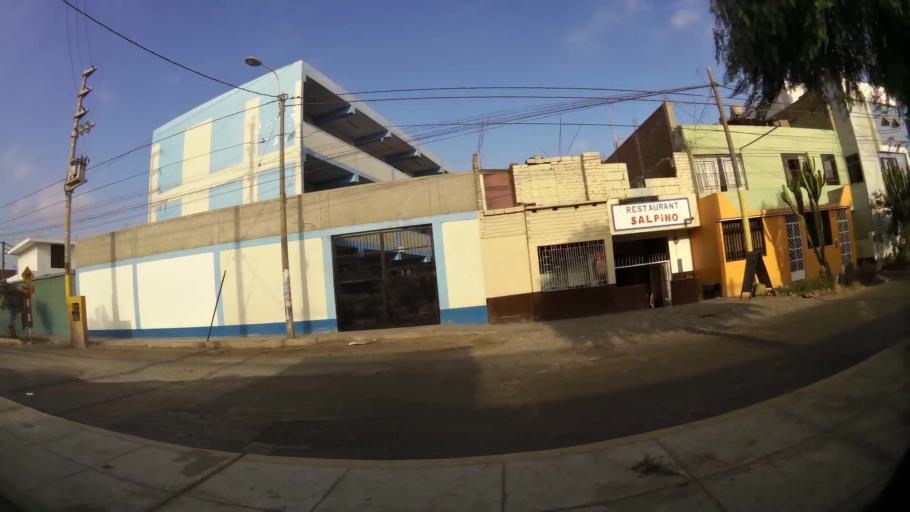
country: PE
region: La Libertad
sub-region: Provincia de Trujillo
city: El Porvenir
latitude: -8.0952
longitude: -79.0155
